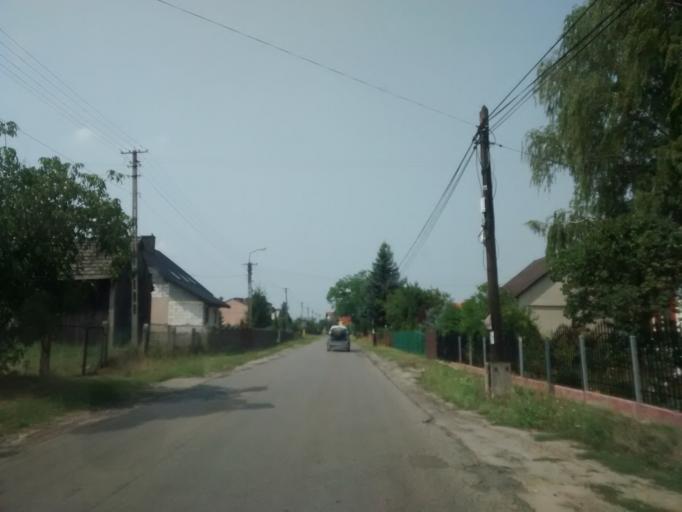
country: PL
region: Lesser Poland Voivodeship
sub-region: Powiat olkuski
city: Klucze
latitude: 50.3659
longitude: 19.5307
